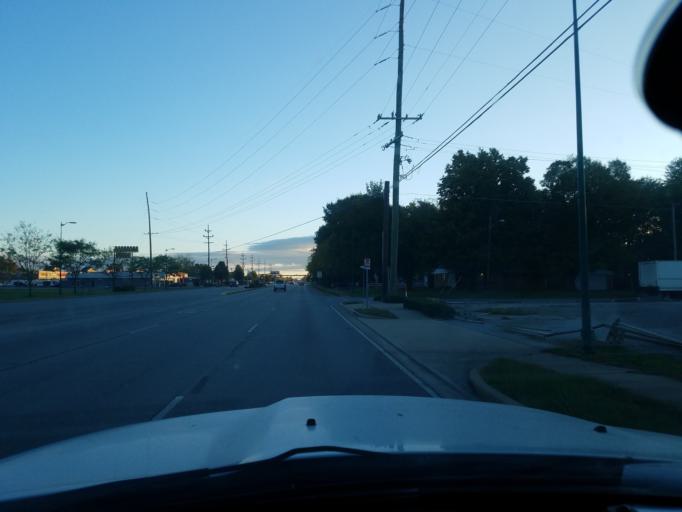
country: US
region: Indiana
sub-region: Clark County
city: Clarksville
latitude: 38.3075
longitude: -85.7737
